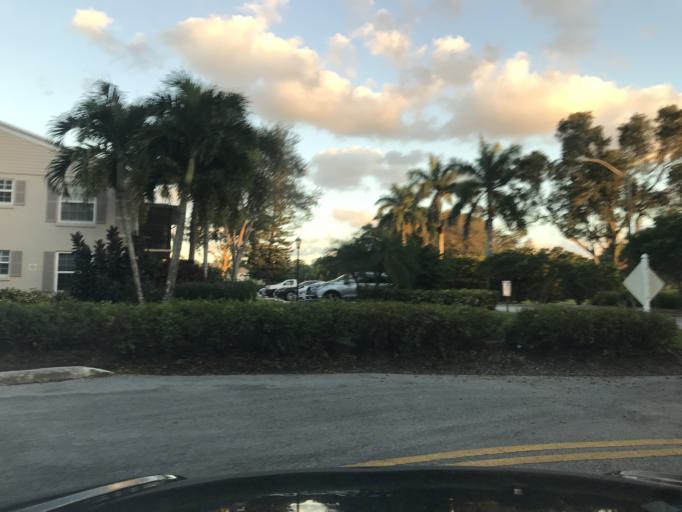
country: US
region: Florida
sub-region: Broward County
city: Pine Island Ridge
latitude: 26.1119
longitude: -80.2710
